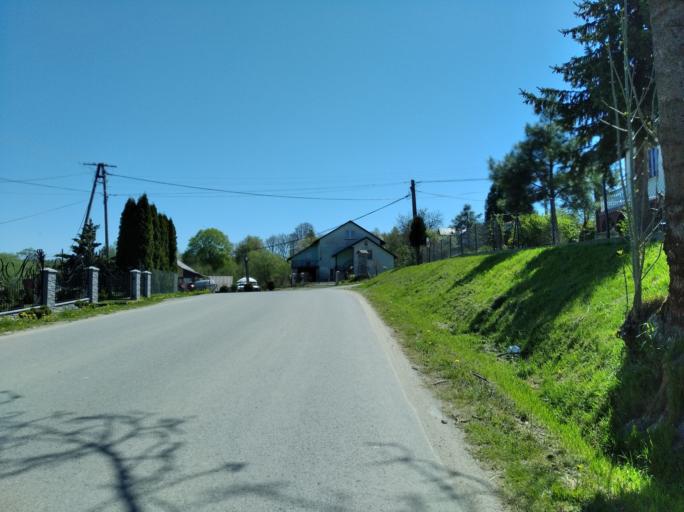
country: PL
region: Subcarpathian Voivodeship
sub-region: Powiat debicki
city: Brzostek
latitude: 49.8990
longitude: 21.4832
